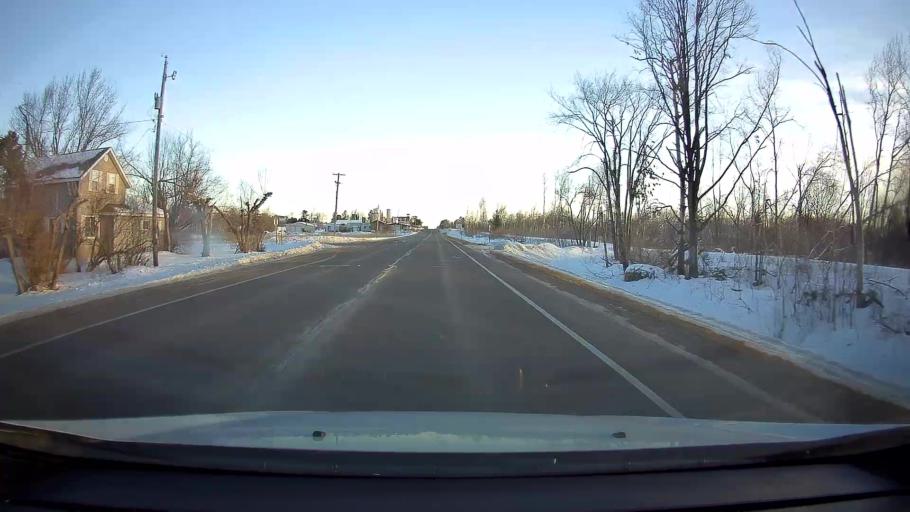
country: US
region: Wisconsin
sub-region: Barron County
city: Cumberland
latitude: 45.4738
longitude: -92.0802
